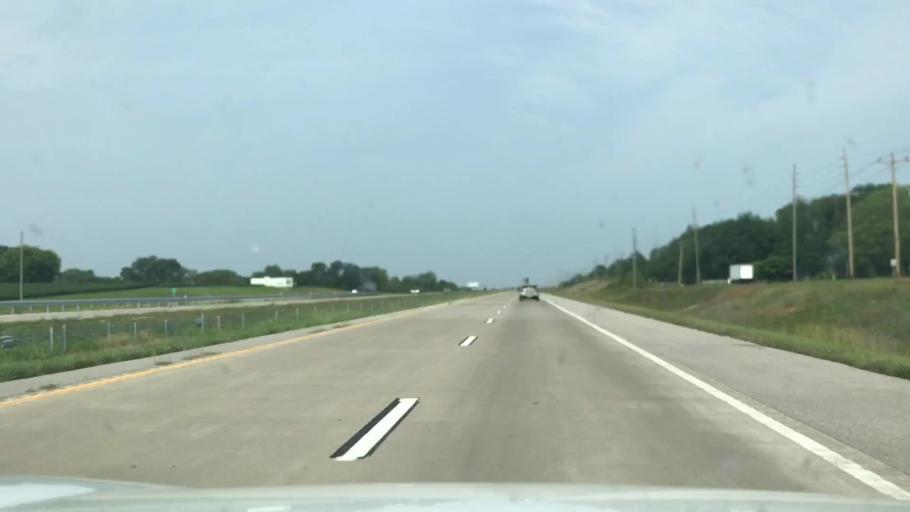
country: US
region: Missouri
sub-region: Saint Charles County
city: Dardenne Prairie
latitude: 38.7619
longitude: -90.7216
